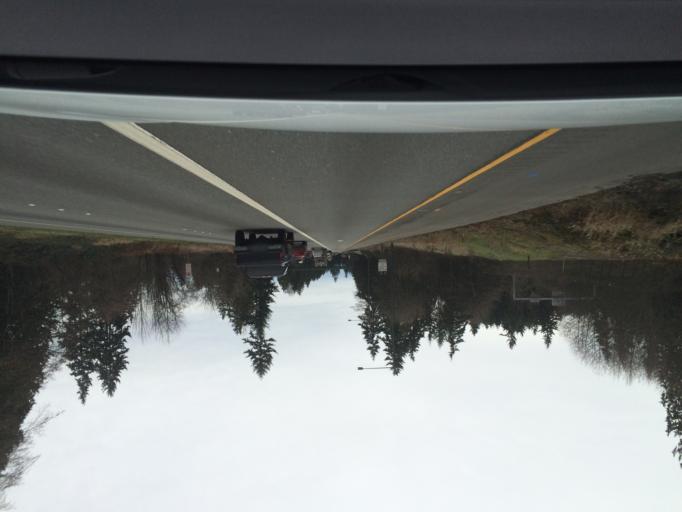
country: US
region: Washington
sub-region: Snohomish County
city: Martha Lake
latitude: 47.8077
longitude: -122.2279
